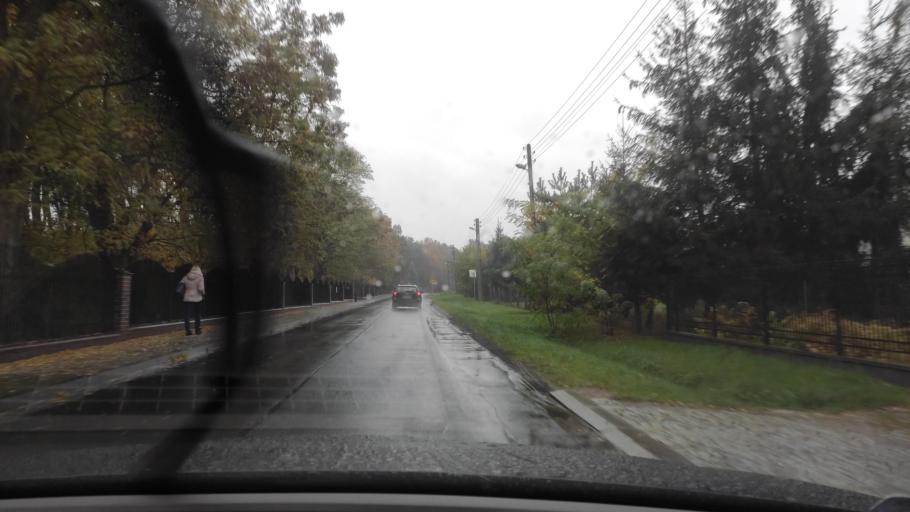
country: PL
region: Greater Poland Voivodeship
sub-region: Powiat poznanski
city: Kornik
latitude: 52.2221
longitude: 17.0971
